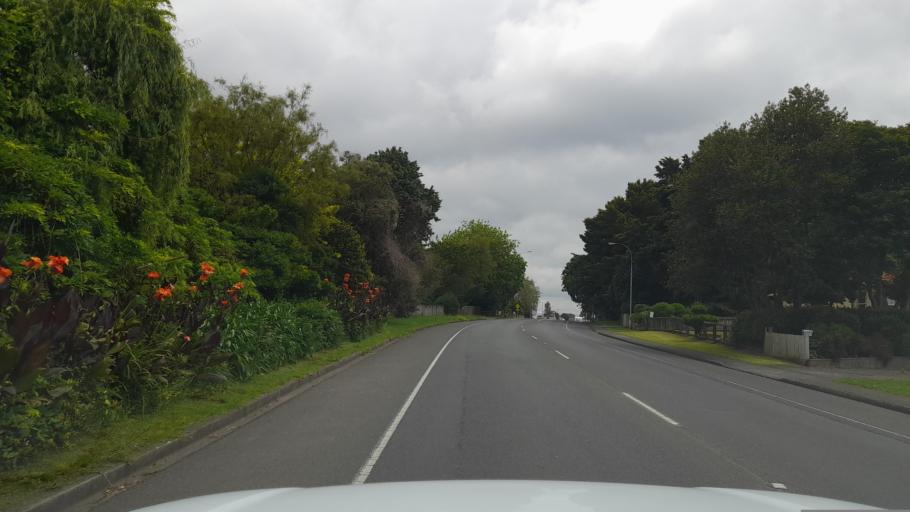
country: NZ
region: Northland
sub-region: Far North District
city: Waimate North
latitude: -35.4040
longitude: 173.8069
